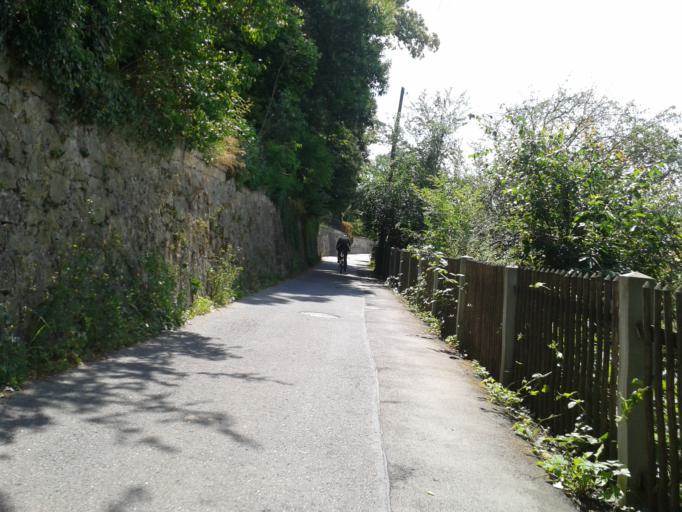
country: DE
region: Saxony
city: Albertstadt
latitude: 51.0568
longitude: 13.8118
